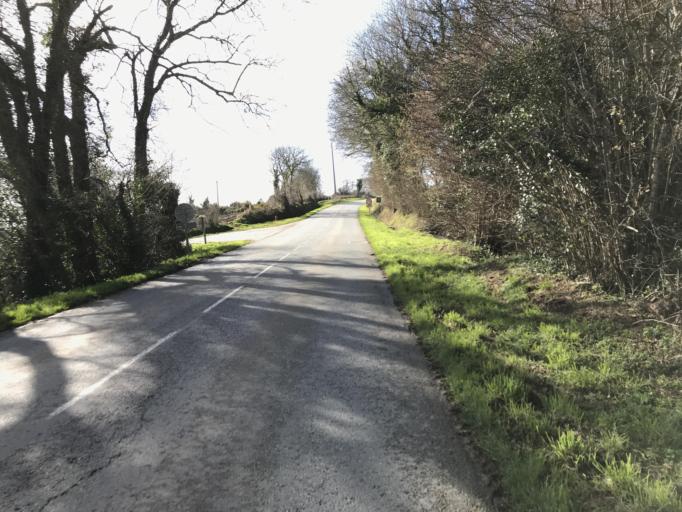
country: FR
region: Brittany
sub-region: Departement du Finistere
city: Loperhet
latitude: 48.3792
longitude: -4.3245
